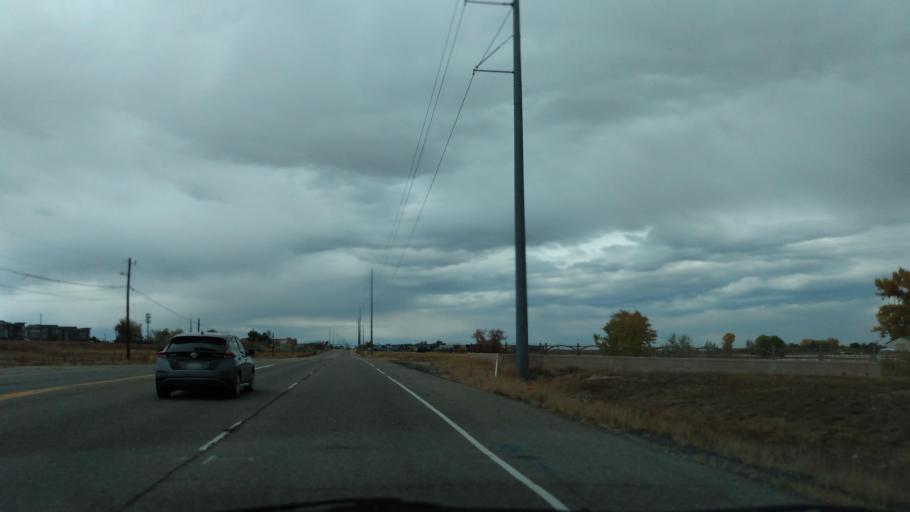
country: US
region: Colorado
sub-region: Adams County
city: Northglenn
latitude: 39.9498
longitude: -104.9782
